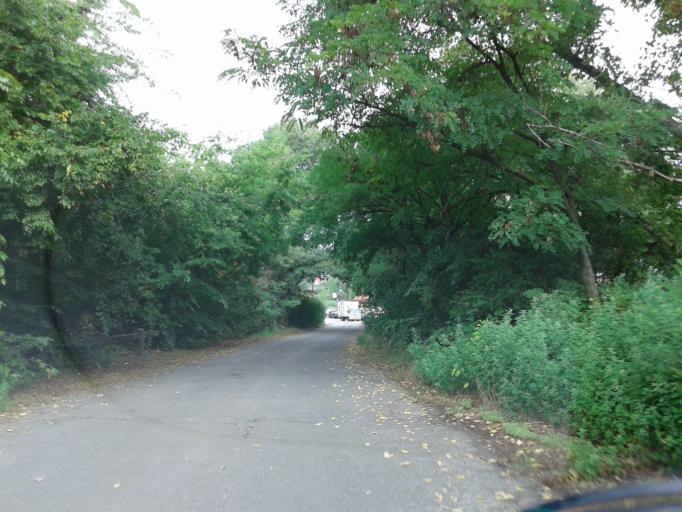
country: HU
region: Csongrad
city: Szeged
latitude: 46.2666
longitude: 20.1239
